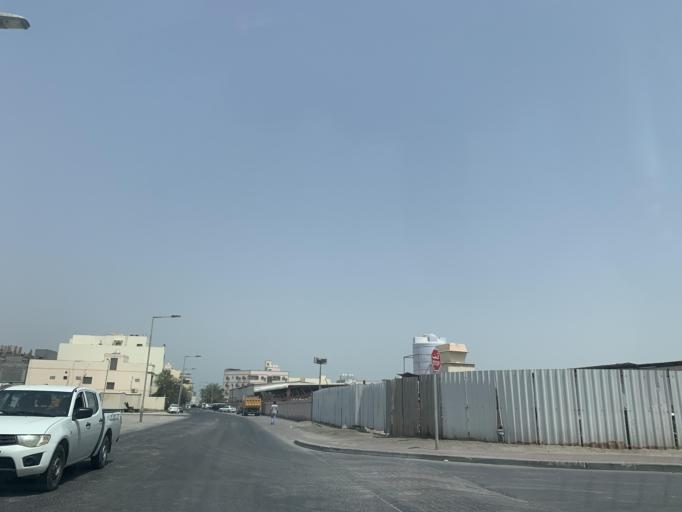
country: BH
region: Northern
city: Madinat `Isa
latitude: 26.1869
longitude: 50.5537
